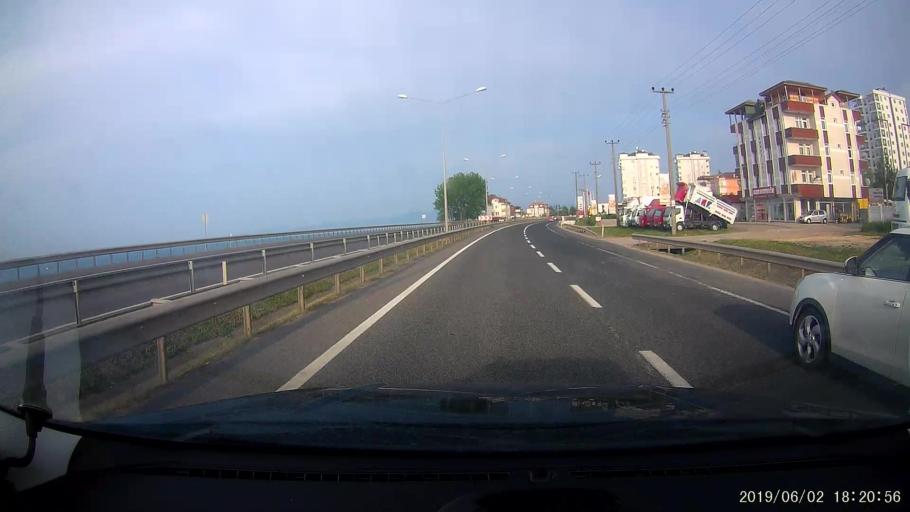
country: TR
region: Ordu
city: Fatsa
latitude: 41.0688
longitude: 37.4605
